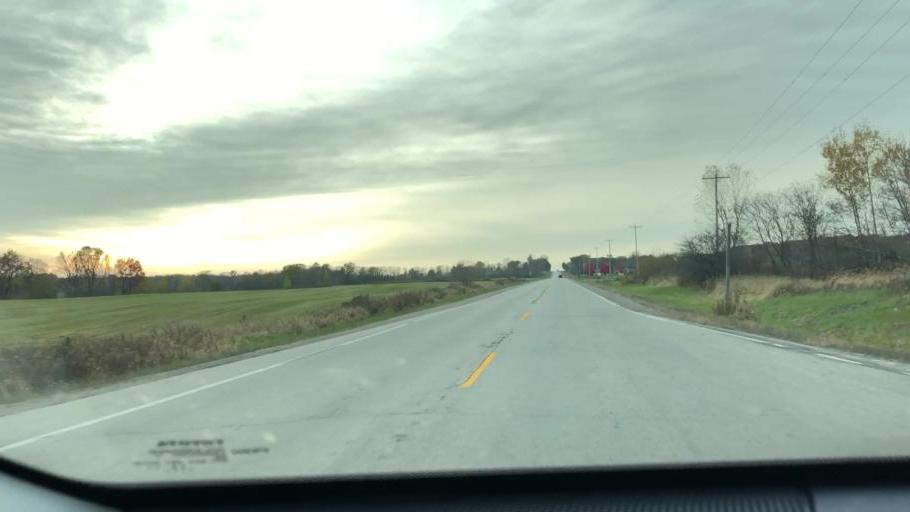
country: US
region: Wisconsin
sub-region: Brown County
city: Oneida
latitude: 44.4443
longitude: -88.2514
